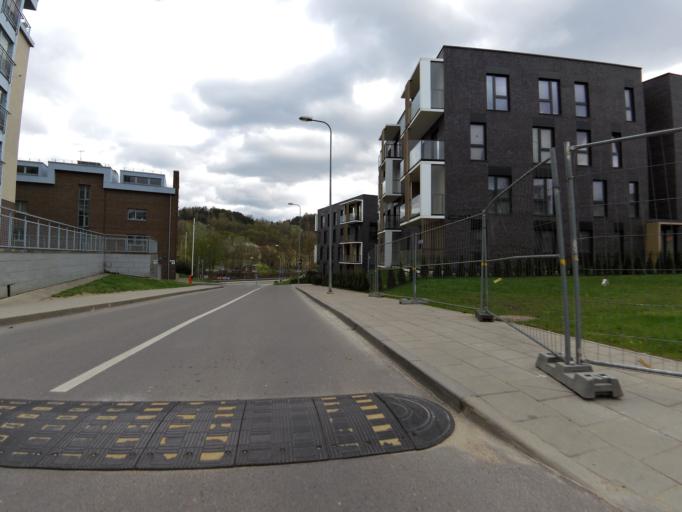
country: LT
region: Vilnius County
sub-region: Vilnius
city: Vilnius
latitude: 54.6926
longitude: 25.2942
